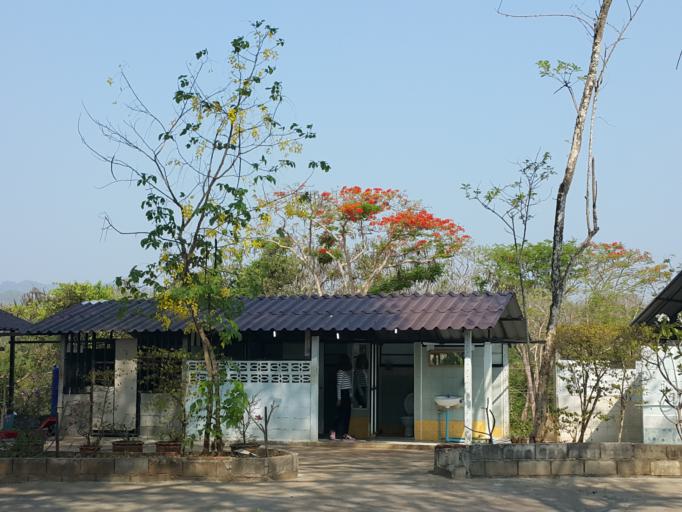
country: TH
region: Kanchanaburi
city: Sai Yok
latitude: 14.1137
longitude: 99.1357
